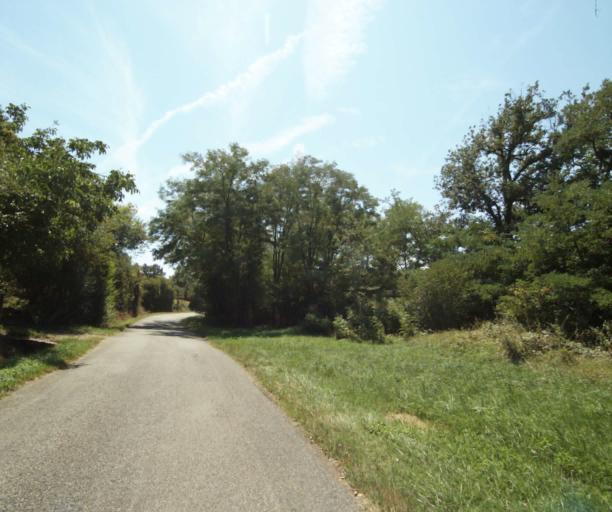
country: FR
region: Midi-Pyrenees
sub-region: Departement de l'Ariege
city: Lezat-sur-Leze
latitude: 43.2715
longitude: 1.3379
